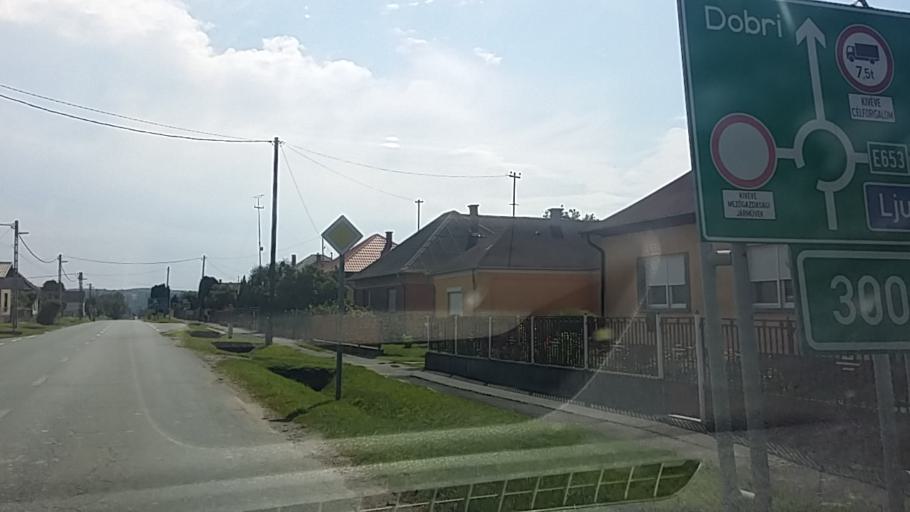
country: HR
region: Medimurska
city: Podturen
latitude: 46.5159
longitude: 16.5577
